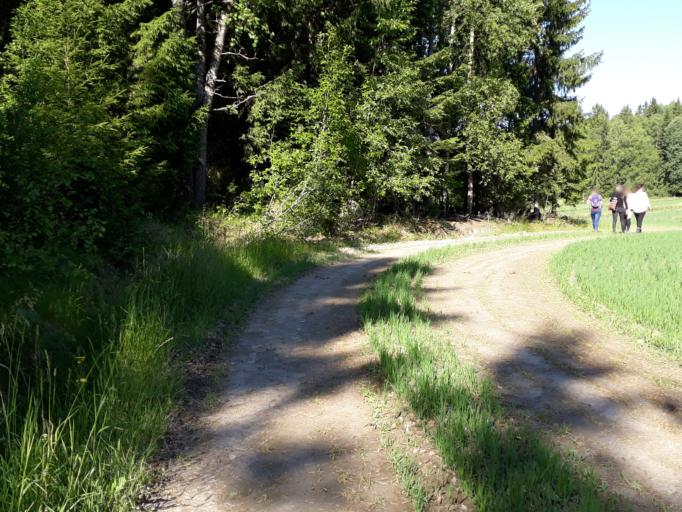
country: FI
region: Uusimaa
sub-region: Helsinki
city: Jaervenpaeae
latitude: 60.5393
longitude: 24.9833
